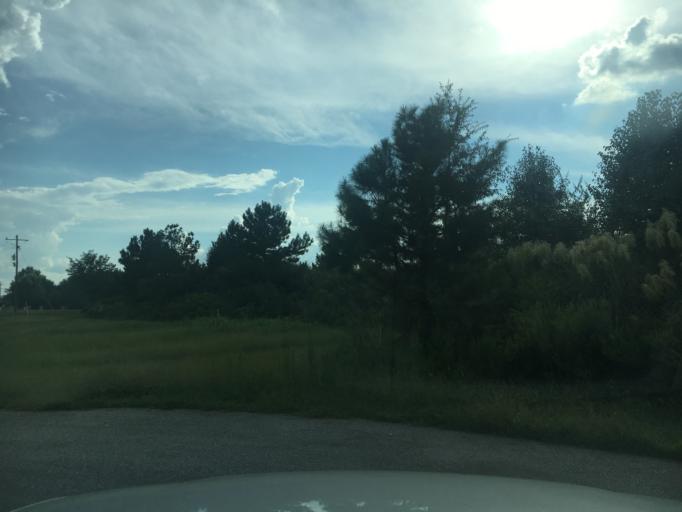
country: US
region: South Carolina
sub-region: Spartanburg County
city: Duncan
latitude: 34.9054
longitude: -82.1692
